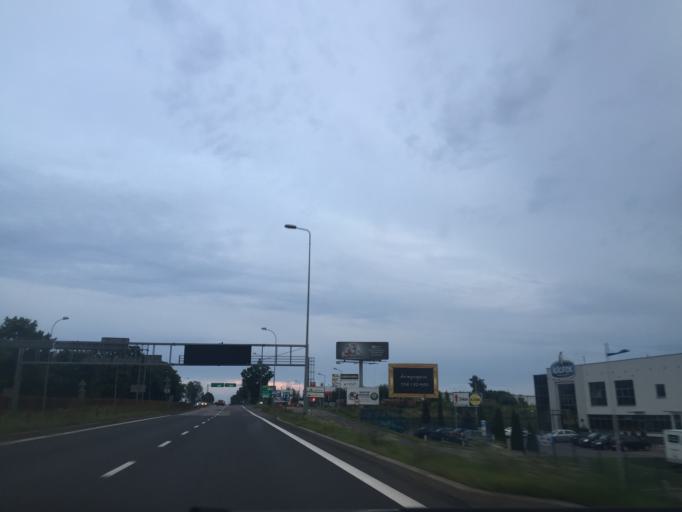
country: PL
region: Podlasie
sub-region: Powiat bialostocki
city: Choroszcz
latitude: 53.1492
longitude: 23.0547
